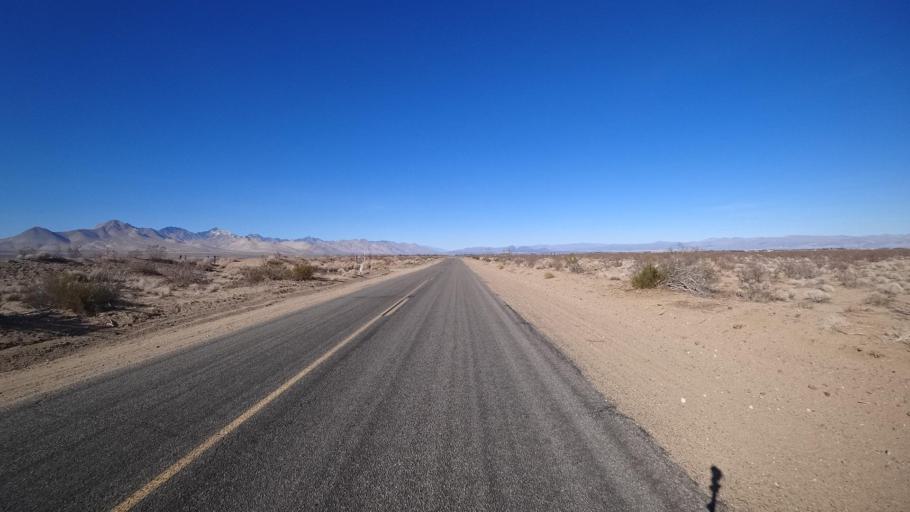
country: US
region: California
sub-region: Kern County
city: Inyokern
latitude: 35.5965
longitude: -117.7965
